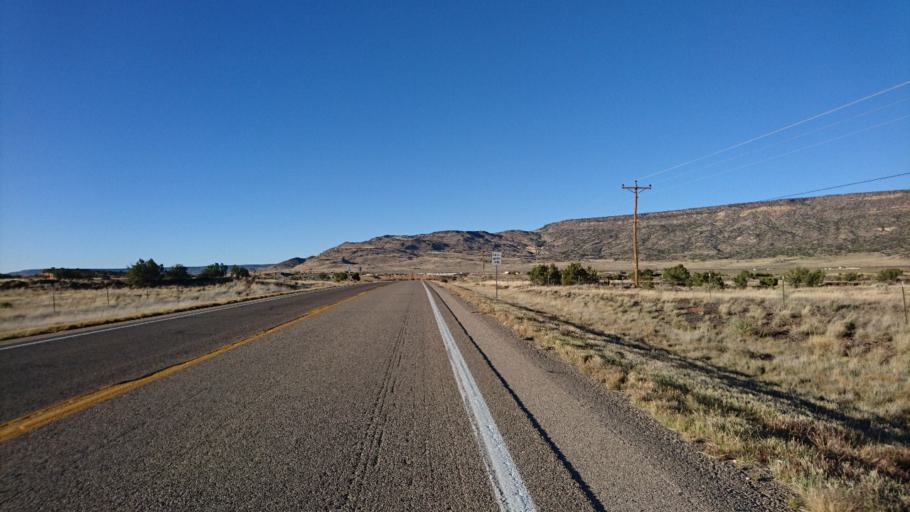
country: US
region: New Mexico
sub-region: Cibola County
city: Grants
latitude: 35.0910
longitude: -107.7707
